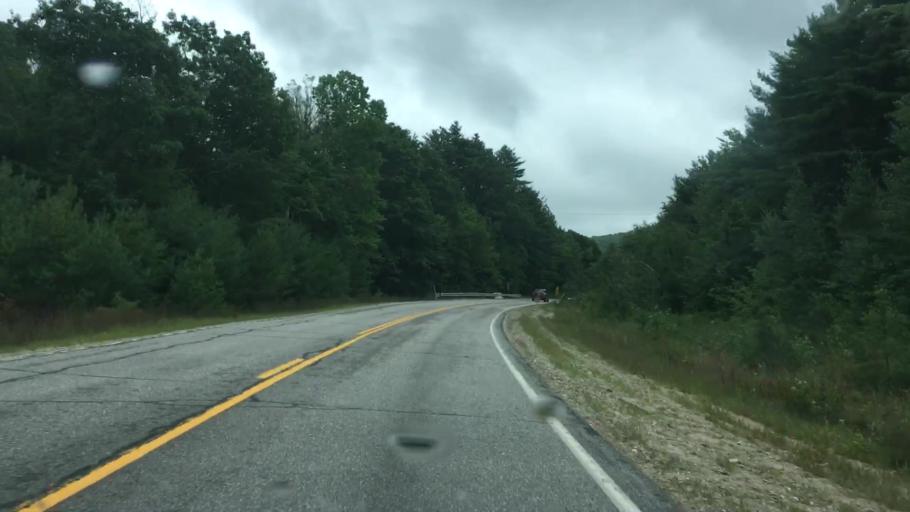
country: US
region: Maine
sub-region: Oxford County
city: Brownfield
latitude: 43.9793
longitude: -70.9271
